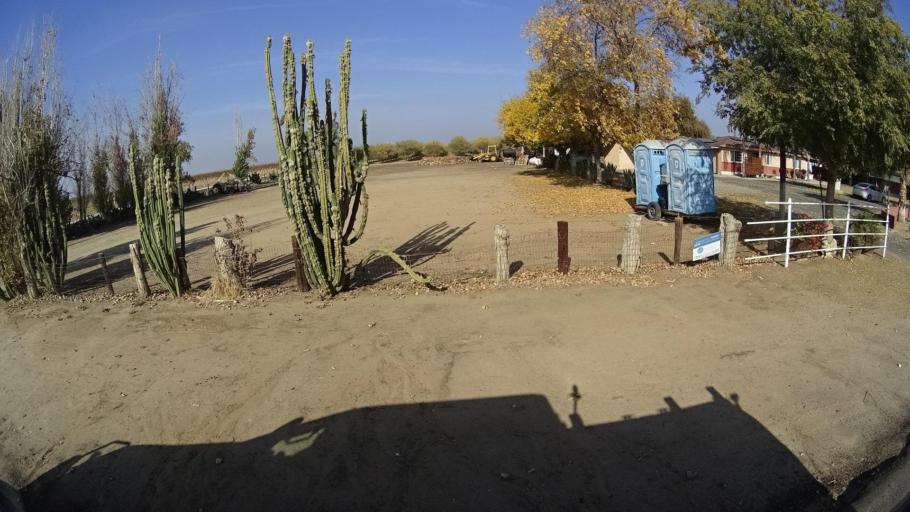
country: US
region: California
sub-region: Kern County
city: McFarland
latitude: 35.6311
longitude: -119.1861
